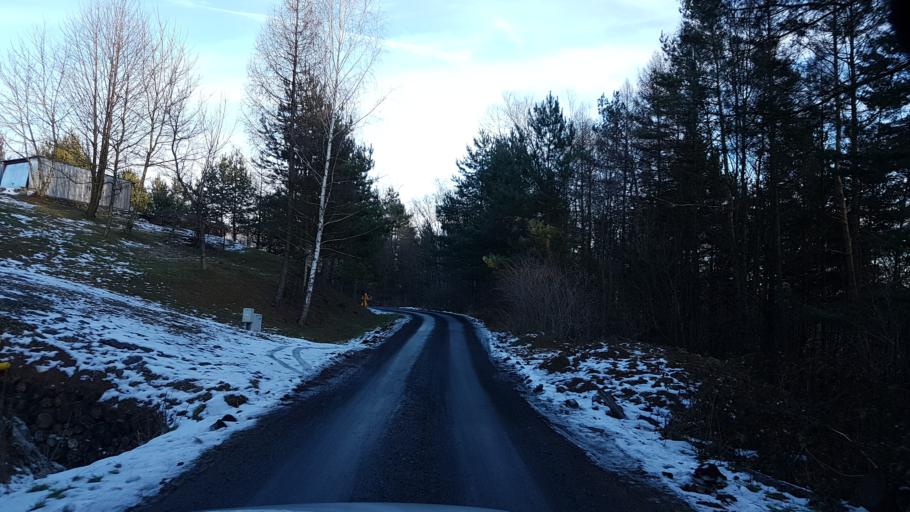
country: PL
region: Lesser Poland Voivodeship
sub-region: Powiat nowosadecki
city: Rytro
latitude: 49.4893
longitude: 20.6561
